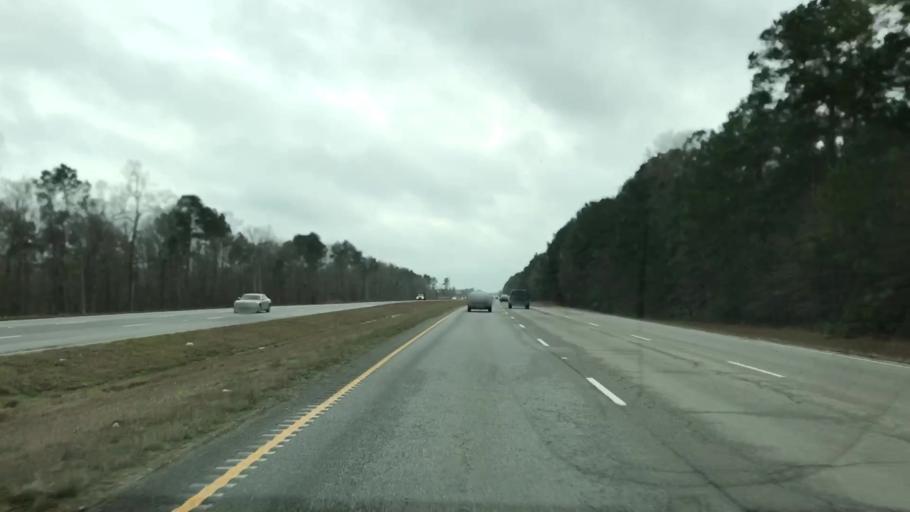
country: US
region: South Carolina
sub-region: Berkeley County
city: Moncks Corner
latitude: 33.1143
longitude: -80.0284
